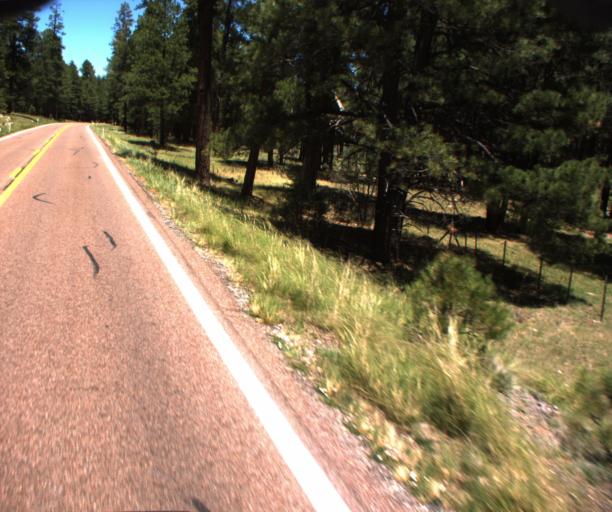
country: US
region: Arizona
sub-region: Gila County
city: Pine
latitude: 34.5270
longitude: -111.3418
